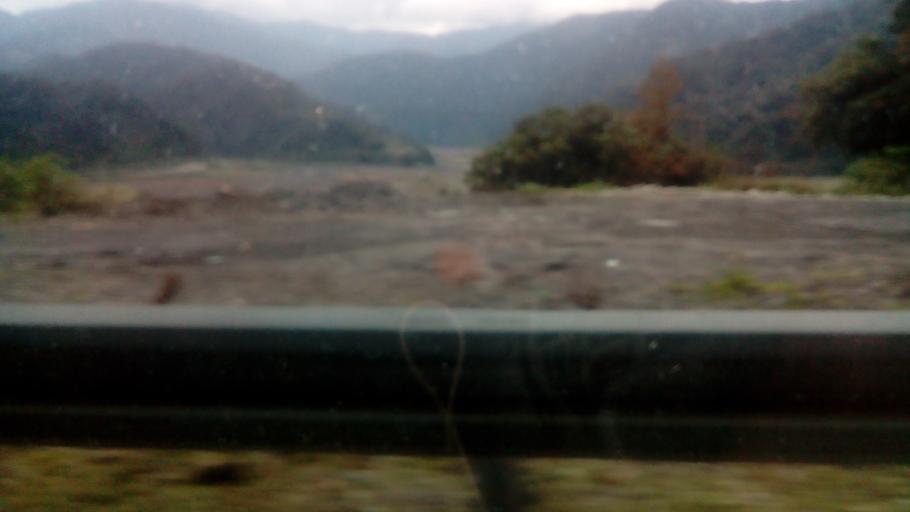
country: TW
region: Taiwan
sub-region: Yilan
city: Yilan
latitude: 24.5844
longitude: 121.4987
